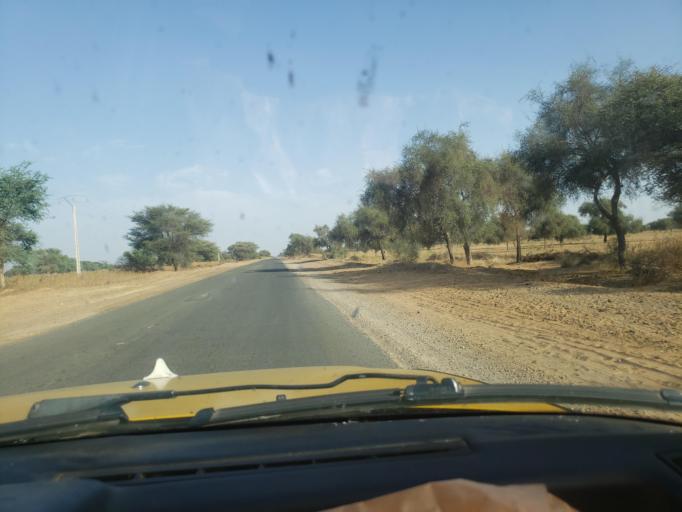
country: SN
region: Louga
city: Louga
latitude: 15.5047
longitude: -15.9561
